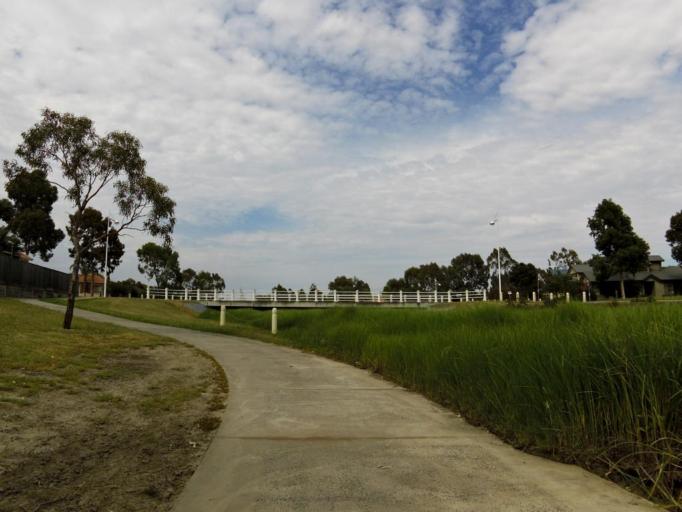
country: AU
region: Victoria
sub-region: Whittlesea
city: Mill Park
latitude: -37.6333
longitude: 145.0711
